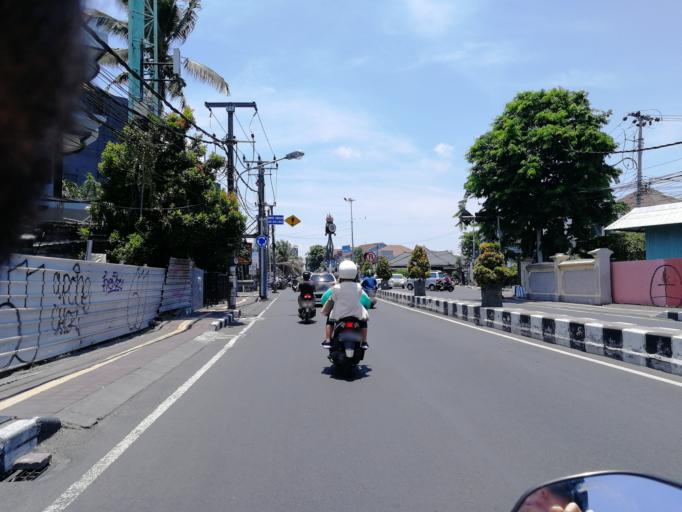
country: ID
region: Bali
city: Denpasar
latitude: -8.6769
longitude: 115.2063
